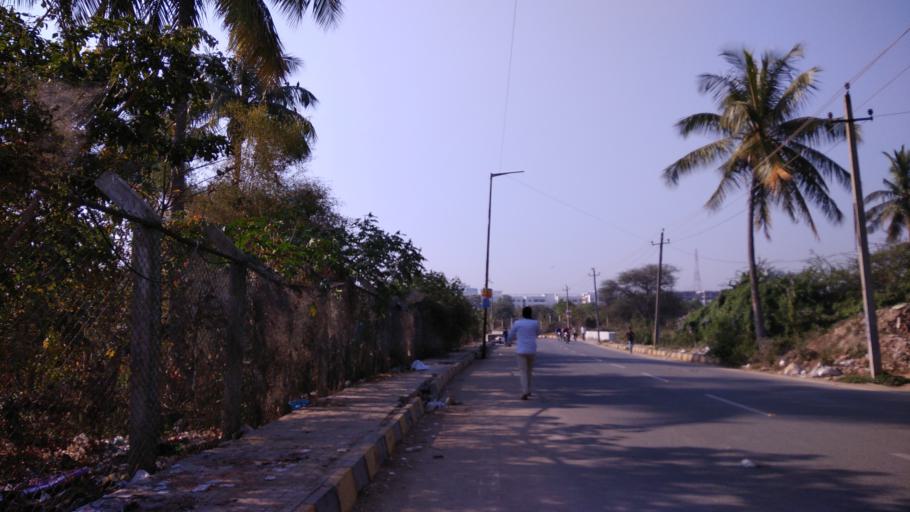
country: IN
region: Karnataka
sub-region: Bangalore Rural
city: Hoskote
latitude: 12.9761
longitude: 77.7336
